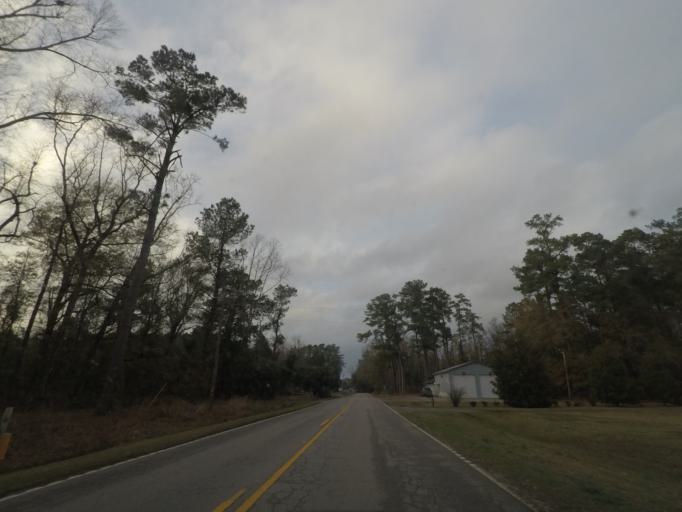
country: US
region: South Carolina
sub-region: Dorchester County
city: Saint George
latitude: 33.0539
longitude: -80.6159
